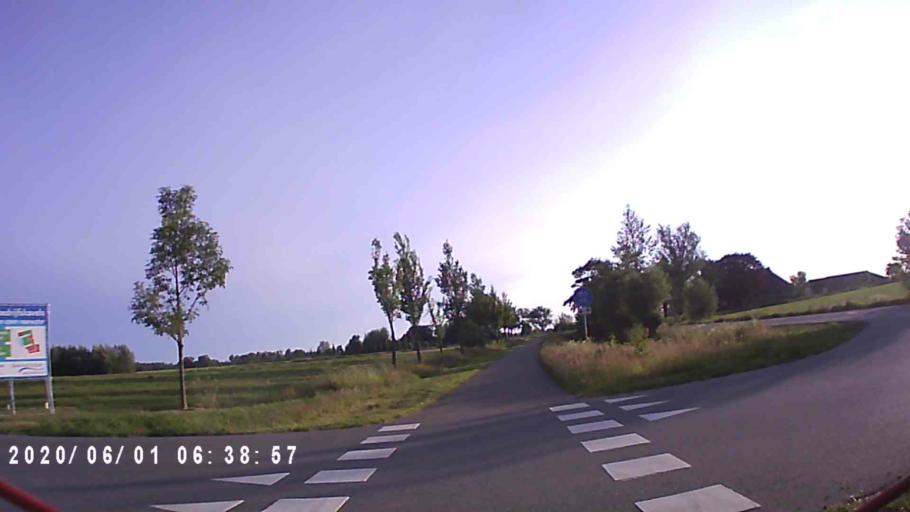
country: NL
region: Friesland
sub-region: Gemeente Kollumerland en Nieuwkruisland
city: Kollum
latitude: 53.2883
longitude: 6.1582
